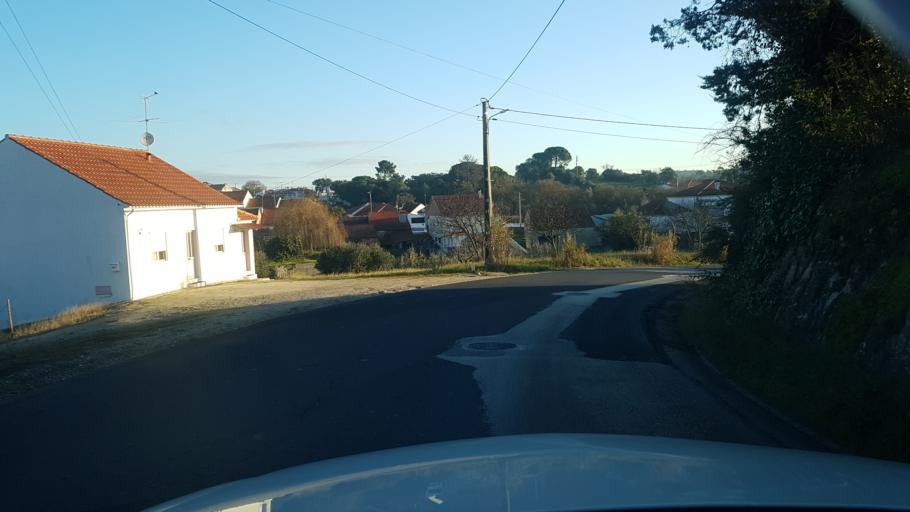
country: PT
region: Santarem
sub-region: Torres Novas
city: Torres Novas
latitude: 39.5532
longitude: -8.5568
